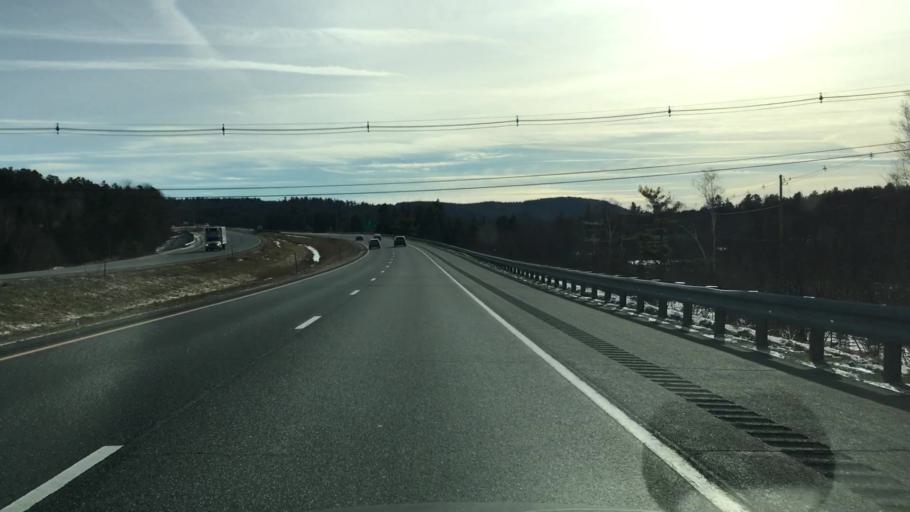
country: US
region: New Hampshire
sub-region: Sullivan County
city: Grantham
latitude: 43.5040
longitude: -72.1345
